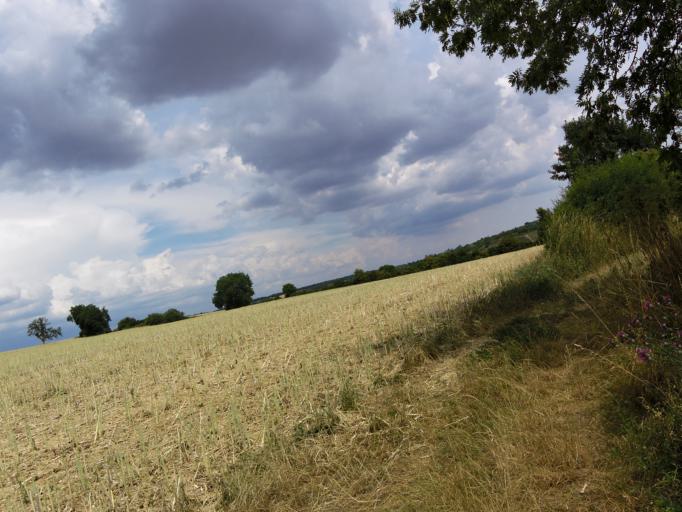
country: DE
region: Bavaria
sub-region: Regierungsbezirk Unterfranken
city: Randersacker
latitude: 49.7658
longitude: 9.9829
